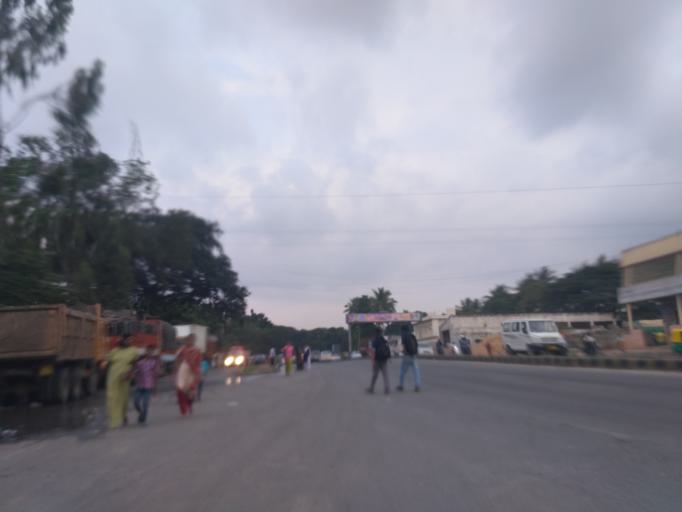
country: IN
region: Karnataka
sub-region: Bangalore Urban
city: Bangalore
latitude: 13.0233
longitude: 77.5330
